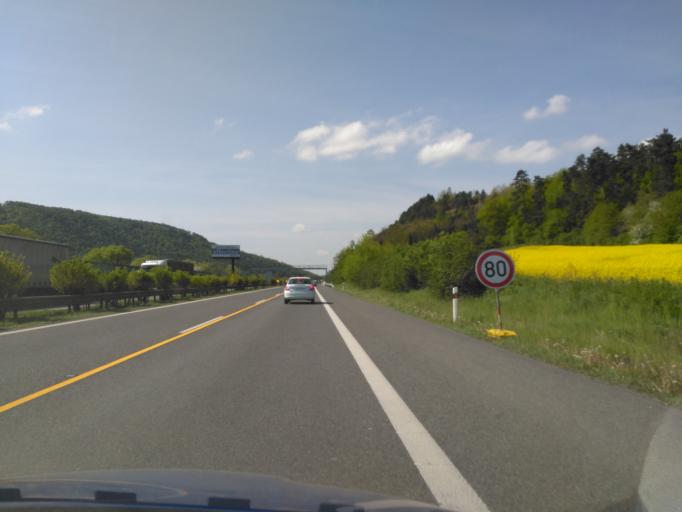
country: CZ
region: Central Bohemia
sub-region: Okres Beroun
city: Kraluv Dvur
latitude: 49.9304
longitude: 14.0157
